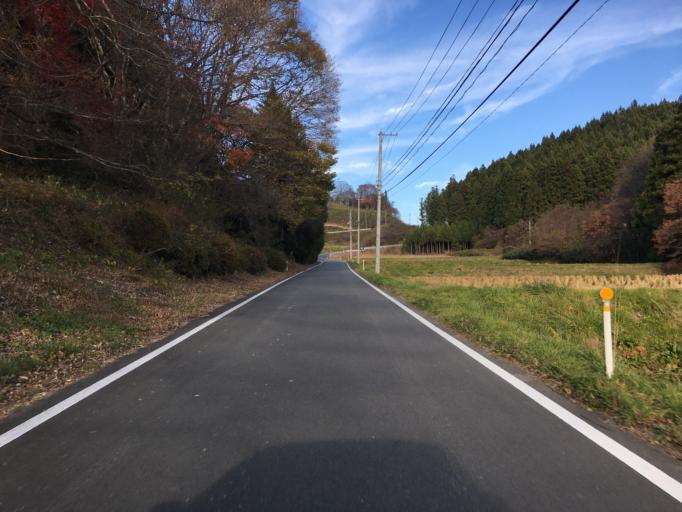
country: JP
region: Fukushima
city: Ishikawa
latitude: 37.2321
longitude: 140.5826
